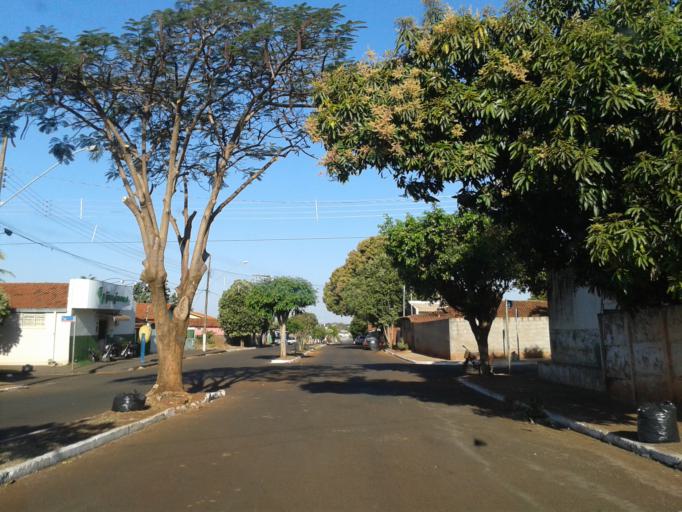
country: BR
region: Minas Gerais
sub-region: Santa Vitoria
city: Santa Vitoria
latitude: -18.8339
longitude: -50.1355
